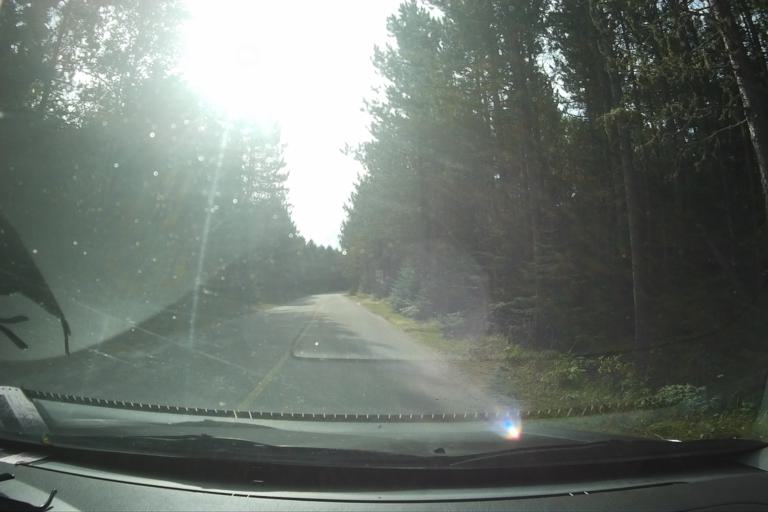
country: CA
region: Ontario
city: Marathon
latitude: 48.7884
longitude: -86.6240
